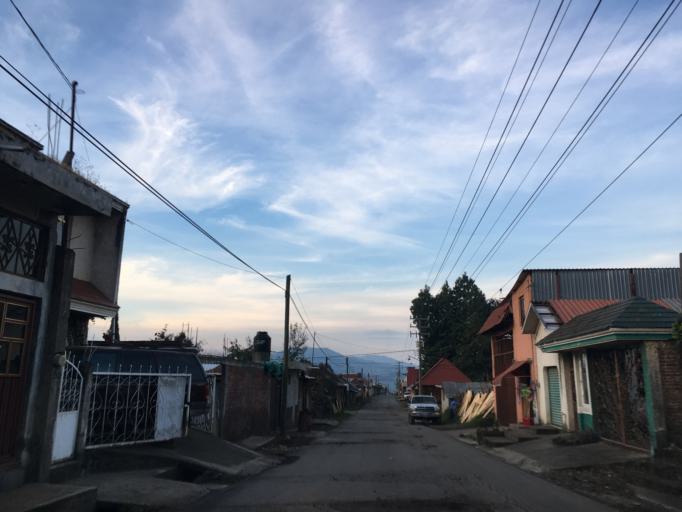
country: MX
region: Michoacan
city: Charapan
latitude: 19.6085
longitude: -102.2334
